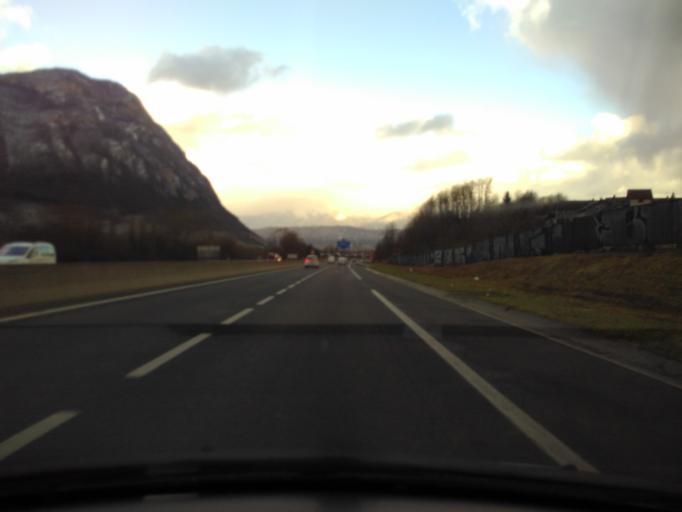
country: FR
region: Rhone-Alpes
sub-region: Departement de la Savoie
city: Les Marches
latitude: 45.5157
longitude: 5.9945
